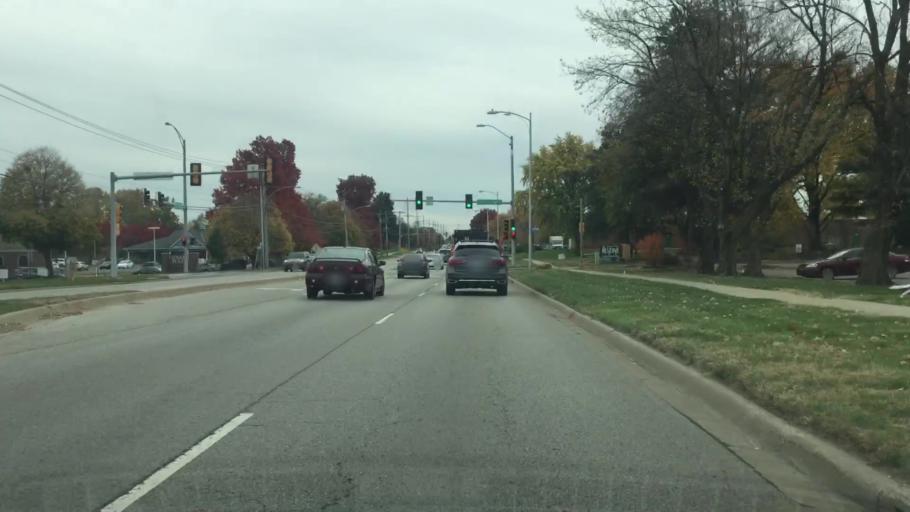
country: US
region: Kansas
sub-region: Johnson County
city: Lenexa
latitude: 38.9884
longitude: -94.7238
